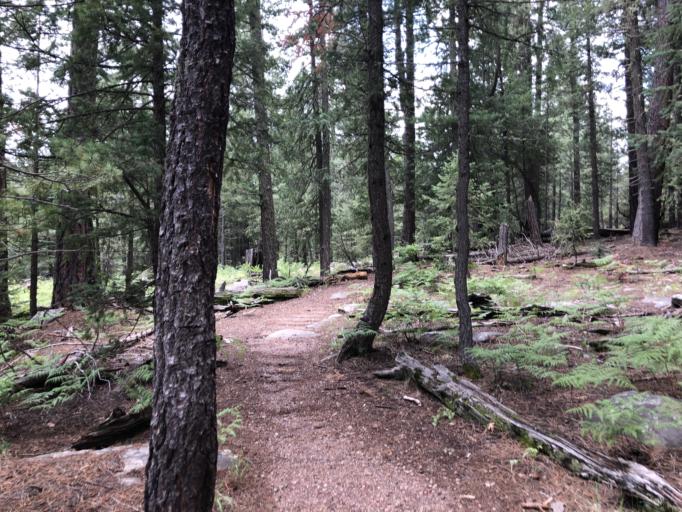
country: US
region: Arizona
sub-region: Gila County
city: Star Valley
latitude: 34.3387
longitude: -110.9526
